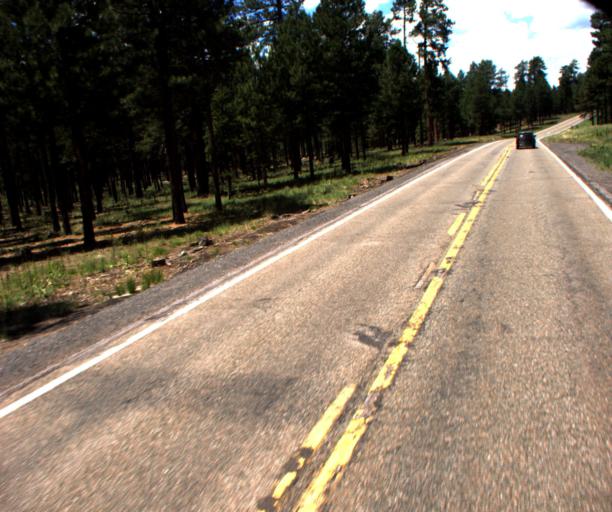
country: US
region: Arizona
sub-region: Coconino County
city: Parks
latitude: 35.3314
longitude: -111.7802
